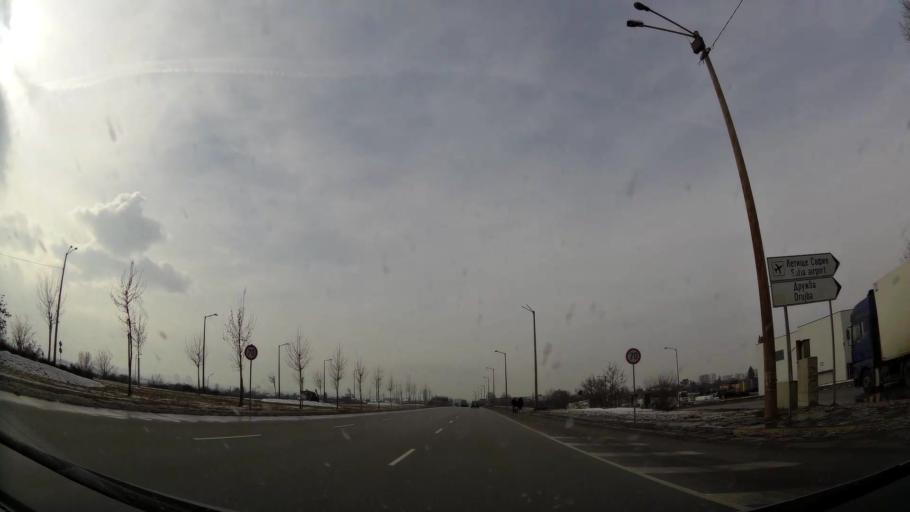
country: BG
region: Sofia-Capital
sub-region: Stolichna Obshtina
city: Sofia
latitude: 42.7047
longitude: 23.3940
